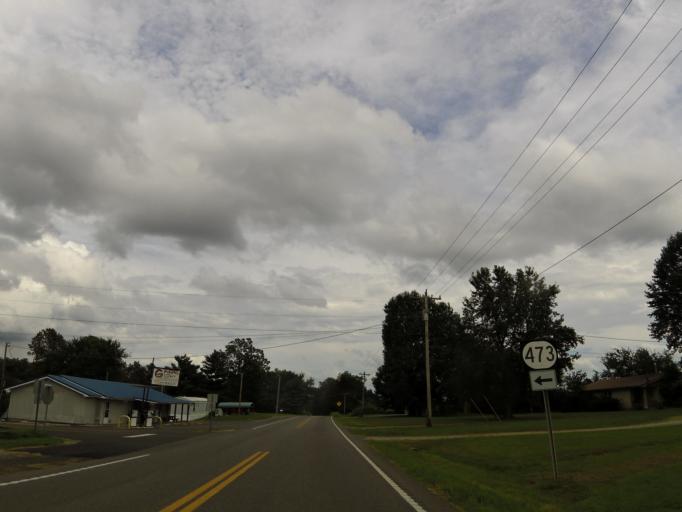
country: US
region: Kentucky
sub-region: Ballard County
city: La Center
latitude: 36.9913
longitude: -88.8900
